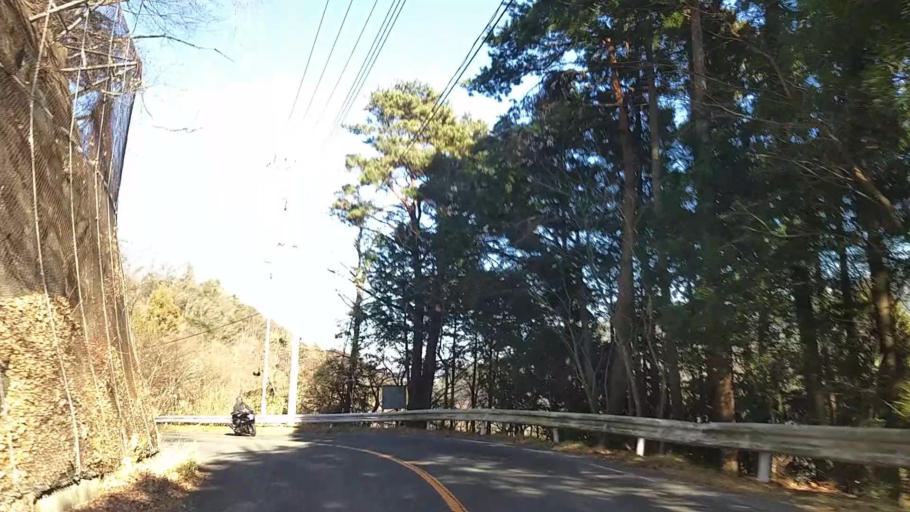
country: JP
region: Yamanashi
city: Uenohara
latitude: 35.5302
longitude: 139.1030
